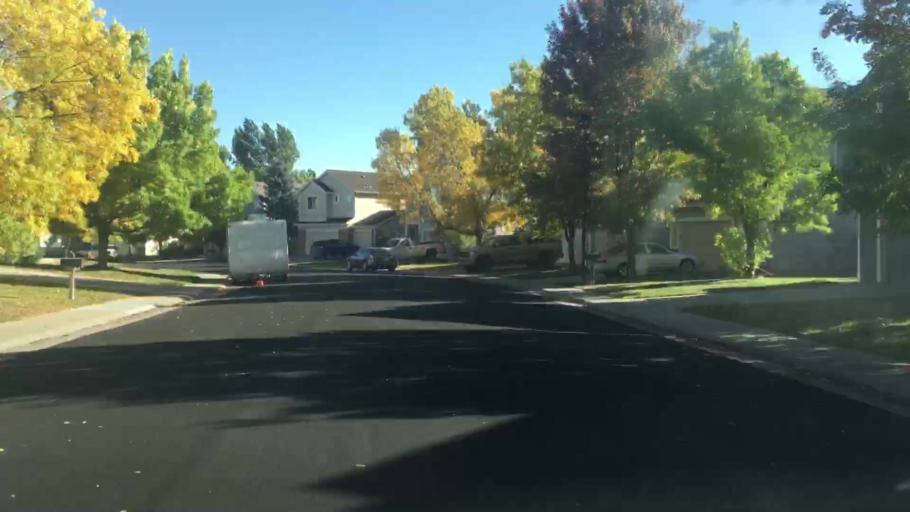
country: US
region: Colorado
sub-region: Douglas County
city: Stonegate
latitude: 39.5171
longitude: -104.7876
